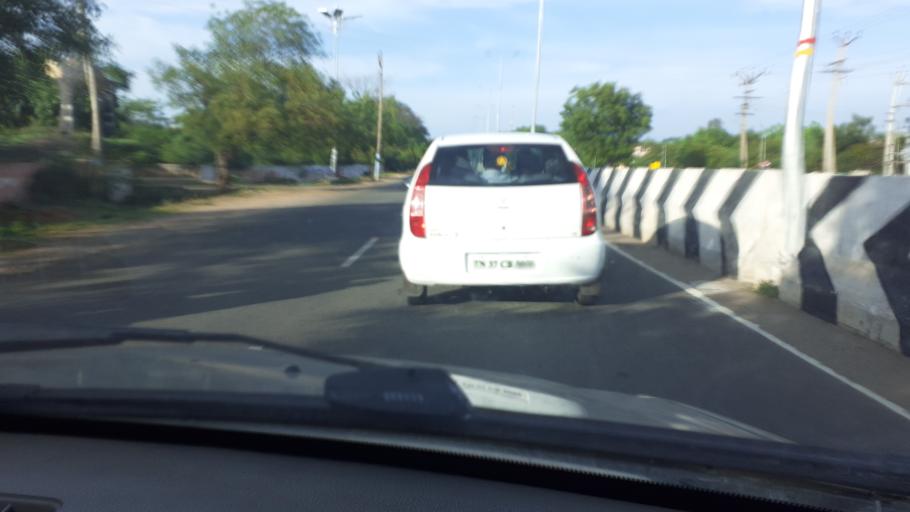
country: IN
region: Tamil Nadu
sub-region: Tirunelveli Kattabo
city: Tirunelveli
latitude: 8.6817
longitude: 77.7237
